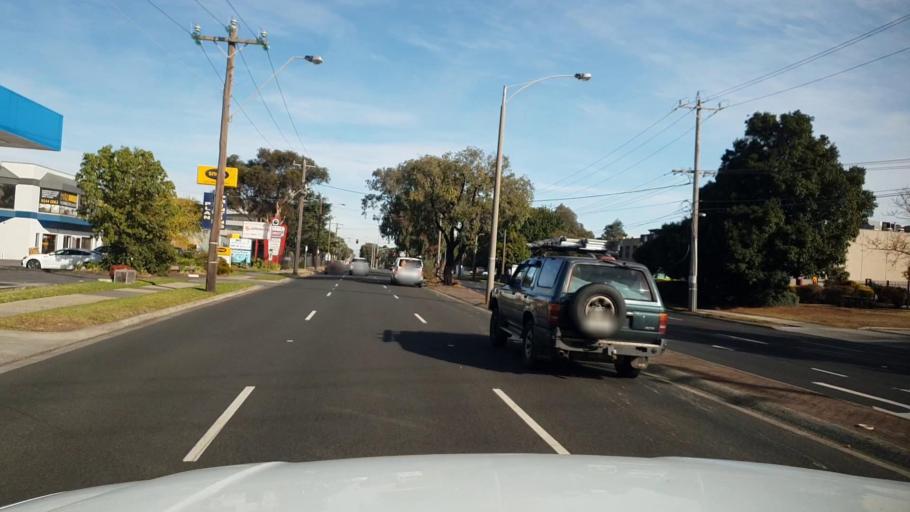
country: AU
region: Victoria
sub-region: Monash
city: Notting Hill
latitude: -37.9008
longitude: 145.1381
